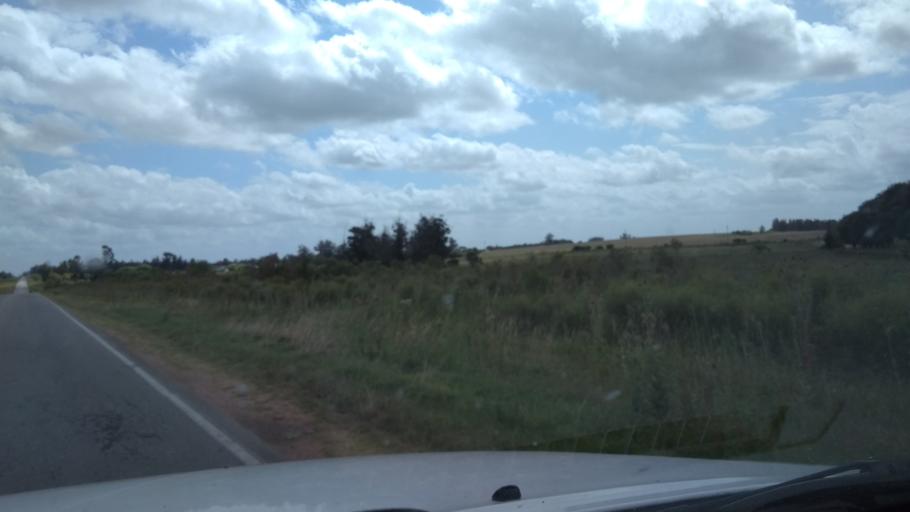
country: UY
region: Canelones
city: San Bautista
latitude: -34.4502
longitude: -55.9791
